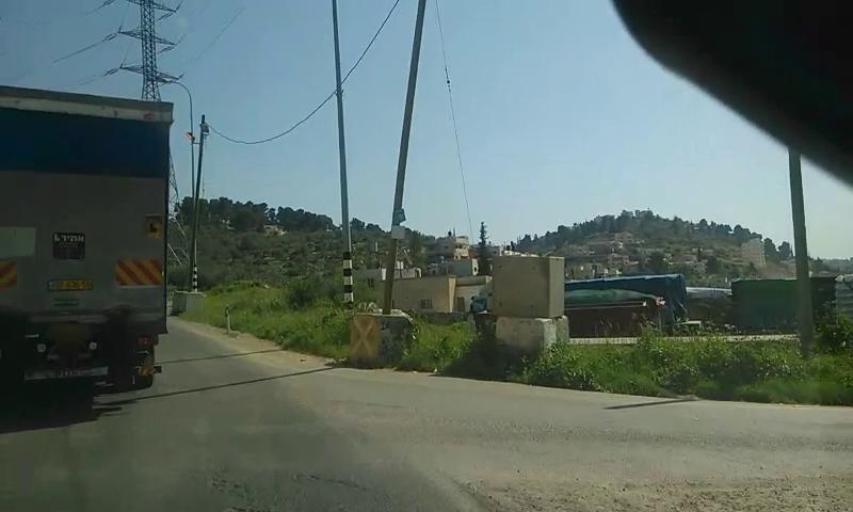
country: PS
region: West Bank
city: Idhna
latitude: 31.5704
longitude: 34.9849
